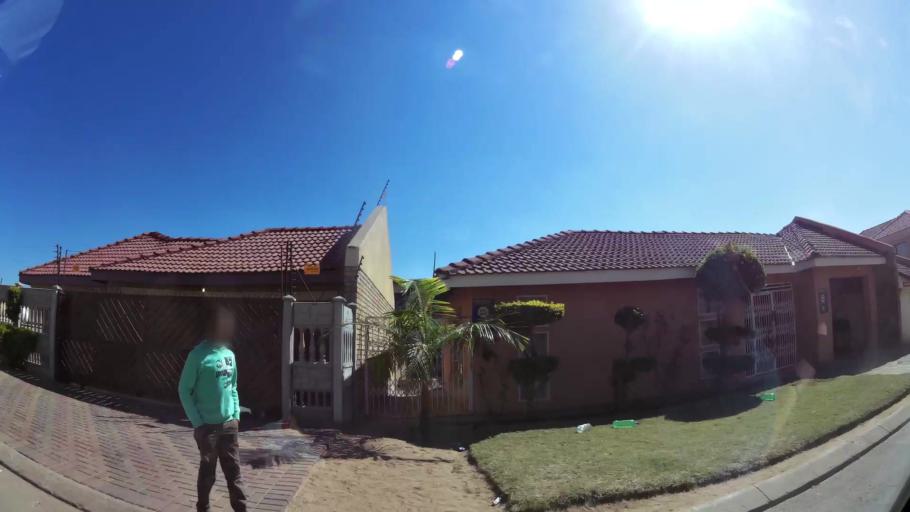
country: ZA
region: Limpopo
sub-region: Capricorn District Municipality
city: Polokwane
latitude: -23.8733
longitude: 29.4102
